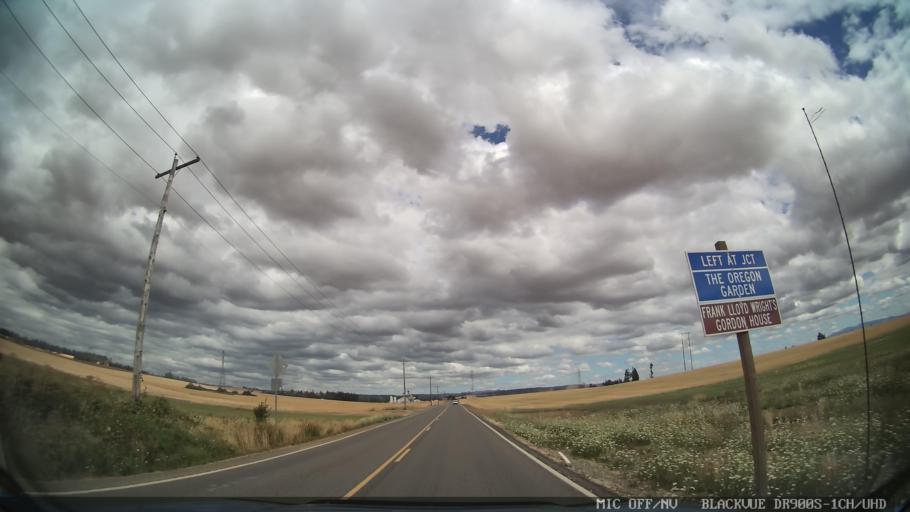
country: US
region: Oregon
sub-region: Marion County
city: Sublimity
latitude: 44.8663
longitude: -122.8003
